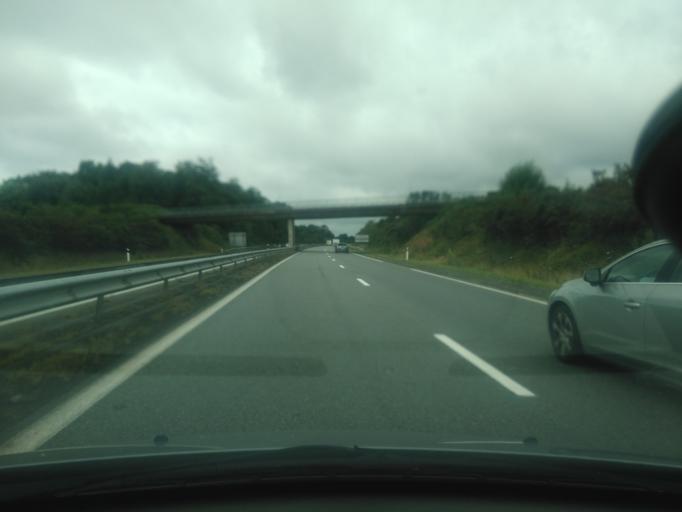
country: FR
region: Brittany
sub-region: Departement des Cotes-d'Armor
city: Trelivan
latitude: 48.4307
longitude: -2.1607
